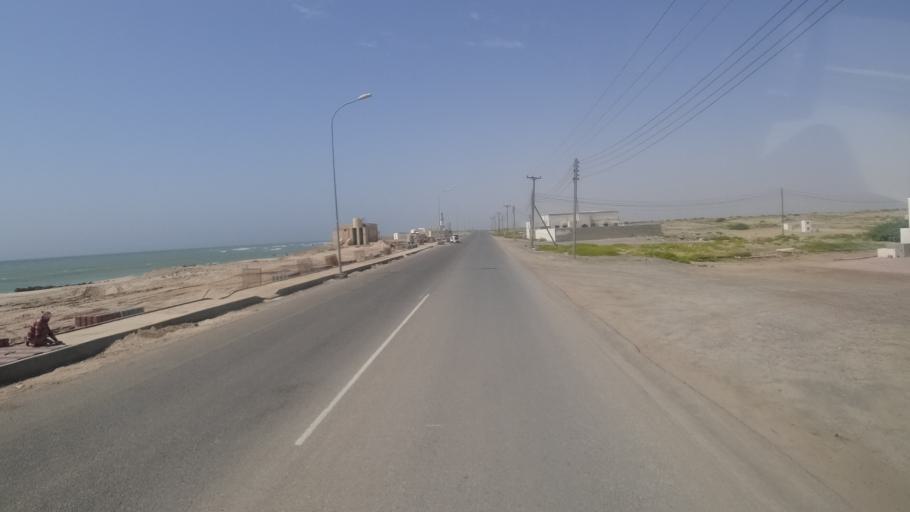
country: OM
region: Ash Sharqiyah
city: Sur
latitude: 22.1134
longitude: 59.7115
